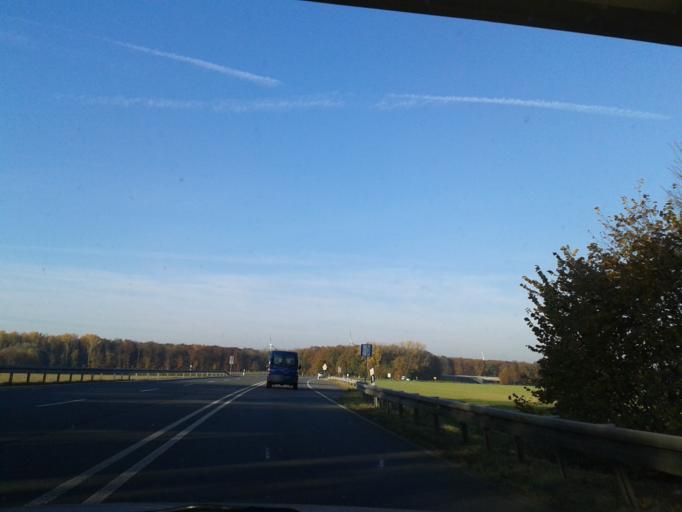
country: DE
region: North Rhine-Westphalia
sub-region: Regierungsbezirk Detmold
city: Salzkotten
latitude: 51.6796
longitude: 8.6487
